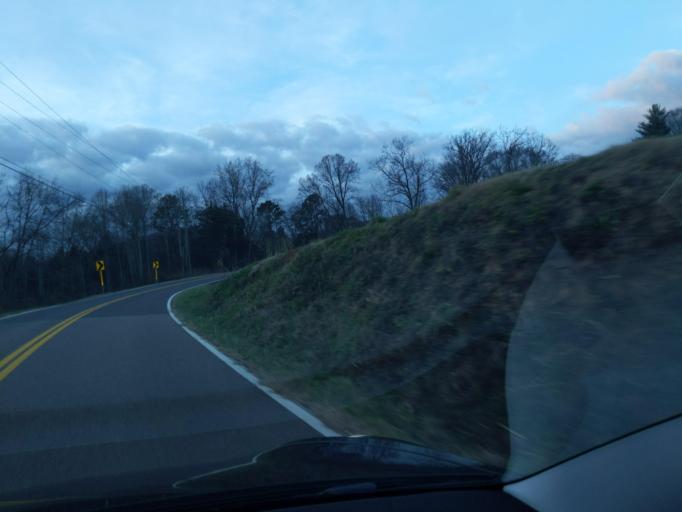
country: US
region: Tennessee
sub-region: Jefferson County
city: White Pine
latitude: 36.1059
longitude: -83.3483
